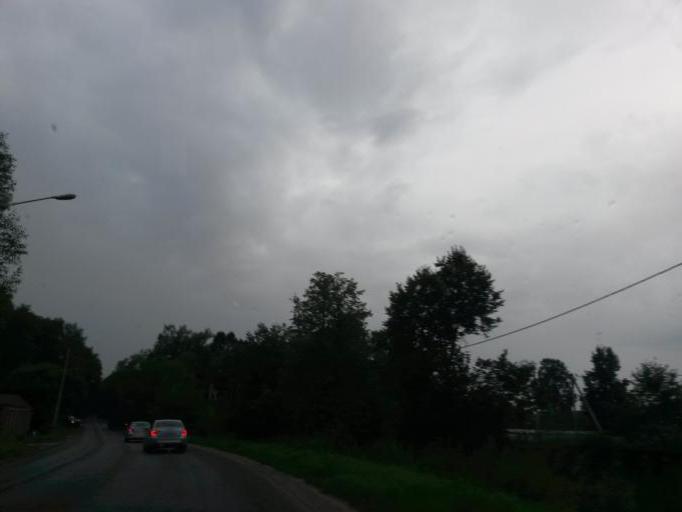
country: RU
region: Moskovskaya
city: Lyubuchany
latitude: 55.2477
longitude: 37.6391
